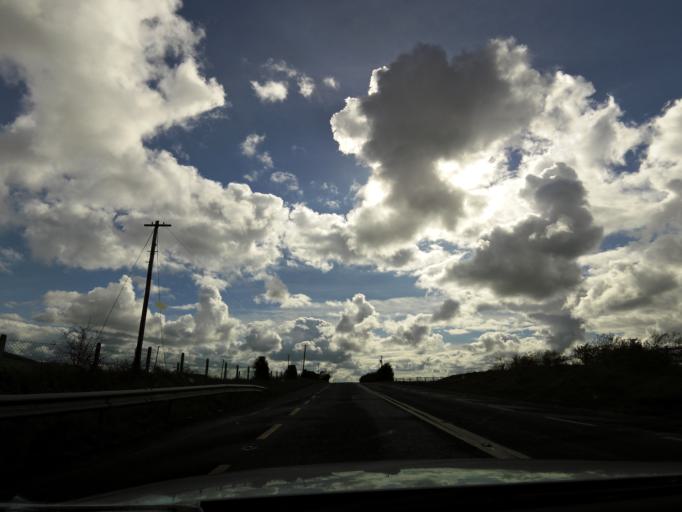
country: IE
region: Leinster
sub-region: Laois
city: Rathdowney
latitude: 52.8028
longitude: -7.5016
